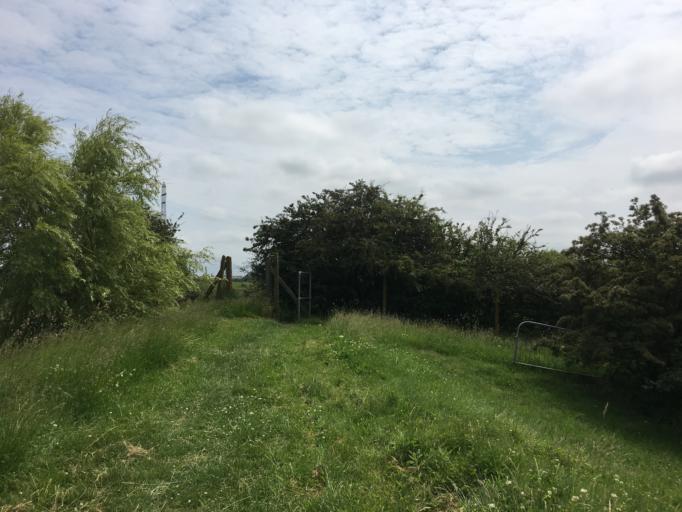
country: GB
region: England
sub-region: Kent
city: Queenborough
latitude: 51.3894
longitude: 0.7490
